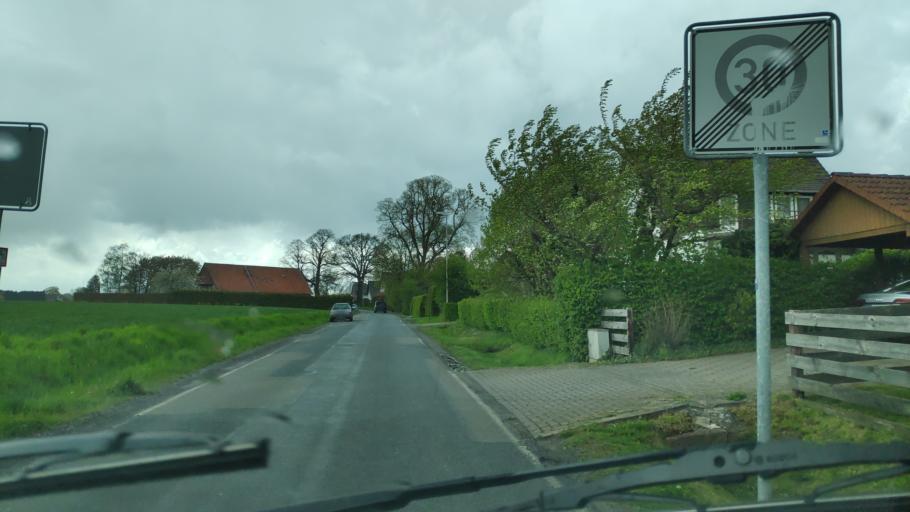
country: DE
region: North Rhine-Westphalia
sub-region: Regierungsbezirk Detmold
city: Minden
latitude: 52.3167
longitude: 8.8995
